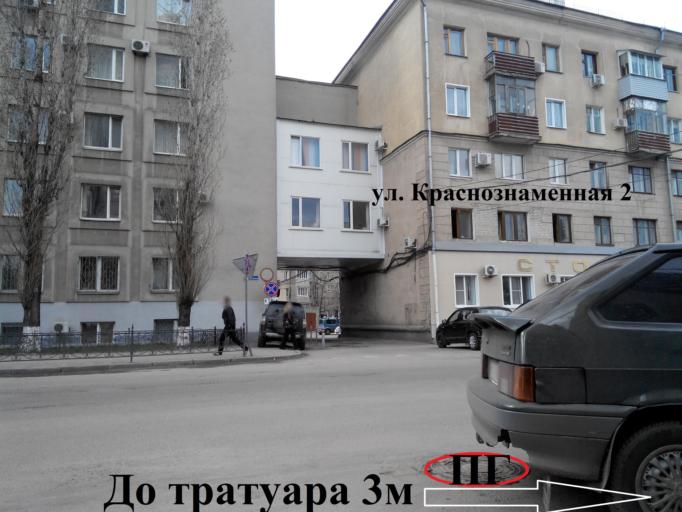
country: RU
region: Voronezj
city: Voronezh
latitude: 51.6545
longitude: 39.1871
